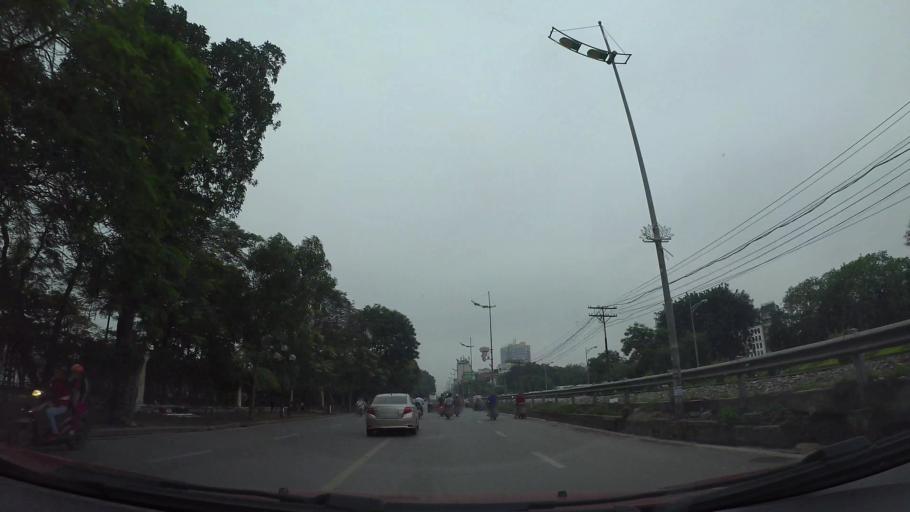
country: VN
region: Ha Noi
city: Hai BaTrung
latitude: 21.0126
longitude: 105.8413
